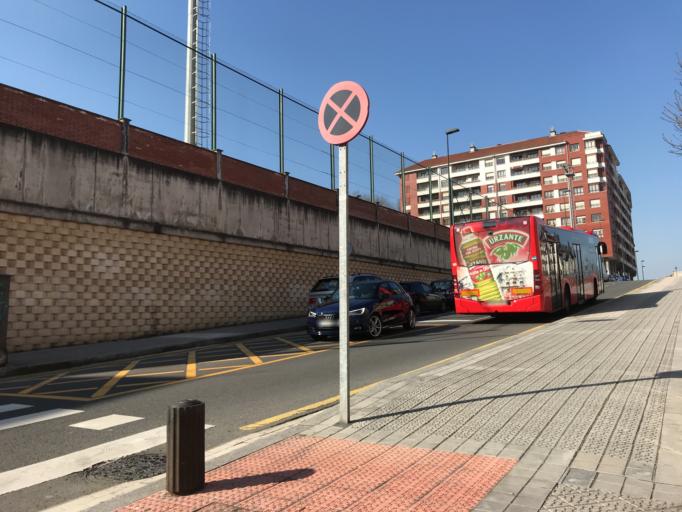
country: ES
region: Basque Country
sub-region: Bizkaia
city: Bilbao
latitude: 43.2570
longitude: -2.9512
